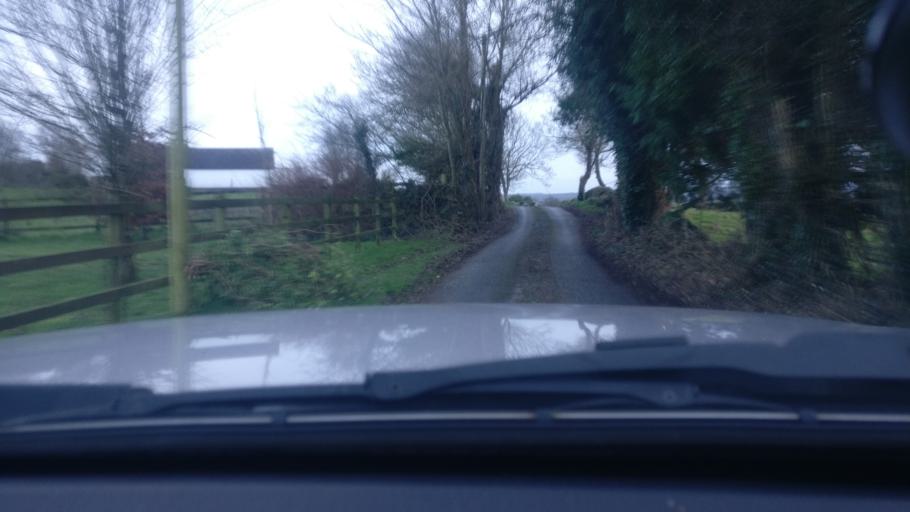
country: IE
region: Connaught
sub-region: County Galway
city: Loughrea
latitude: 53.1845
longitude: -8.6078
